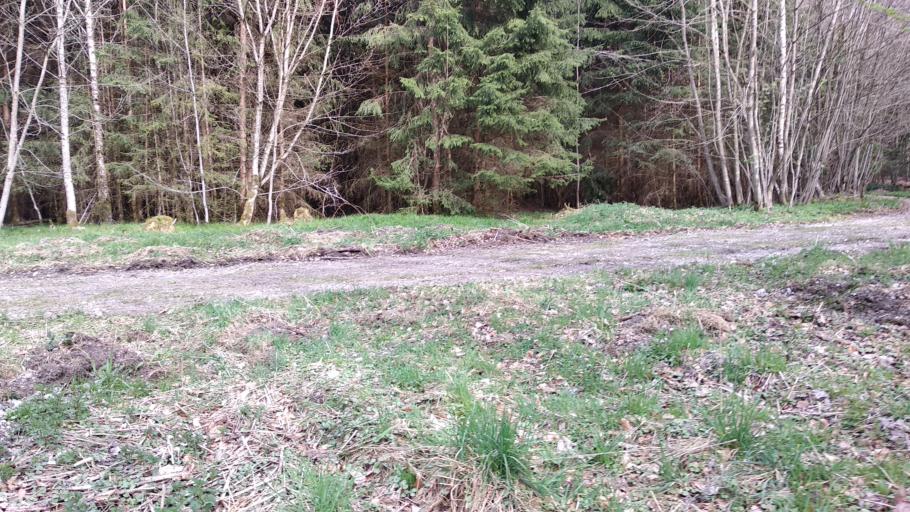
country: DE
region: Bavaria
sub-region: Swabia
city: Kronburg
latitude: 47.9006
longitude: 10.1476
